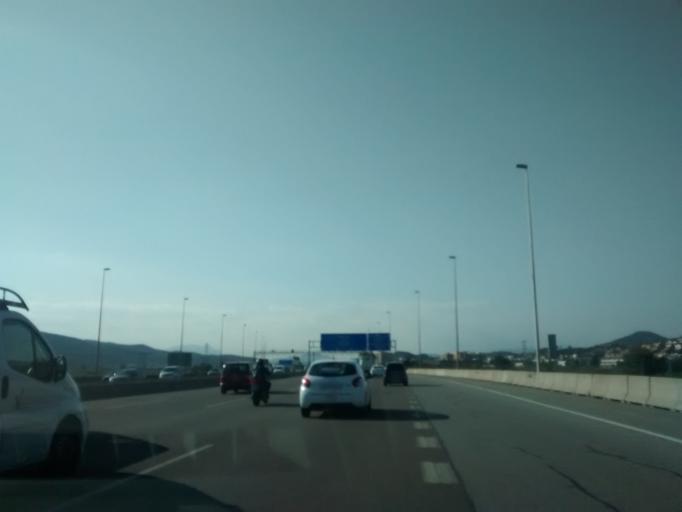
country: ES
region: Catalonia
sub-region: Provincia de Barcelona
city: Sant Vicenc dels Horts
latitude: 41.3962
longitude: 2.0233
